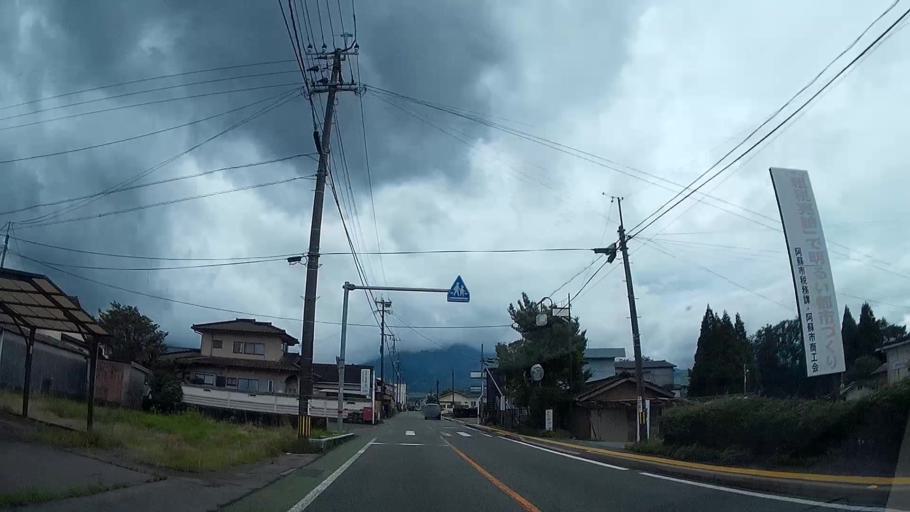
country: JP
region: Kumamoto
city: Aso
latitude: 32.9439
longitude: 131.1178
